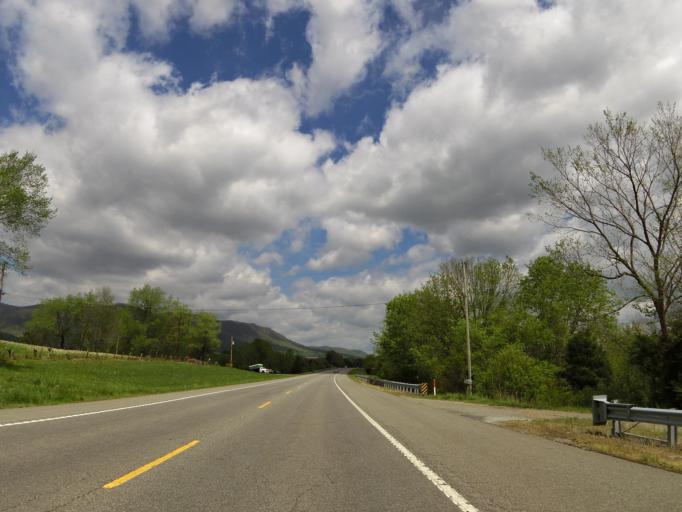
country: US
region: Tennessee
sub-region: Campbell County
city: Fincastle
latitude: 36.4425
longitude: -83.9929
